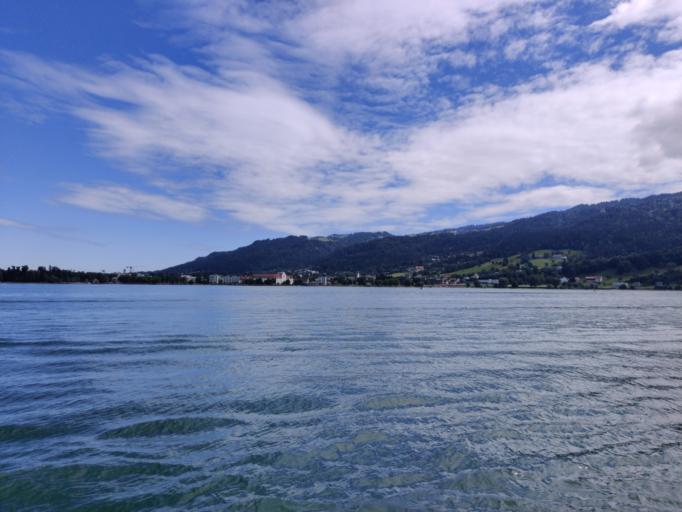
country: AT
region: Vorarlberg
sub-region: Politischer Bezirk Bregenz
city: Bregenz
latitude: 47.5195
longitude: 9.7349
